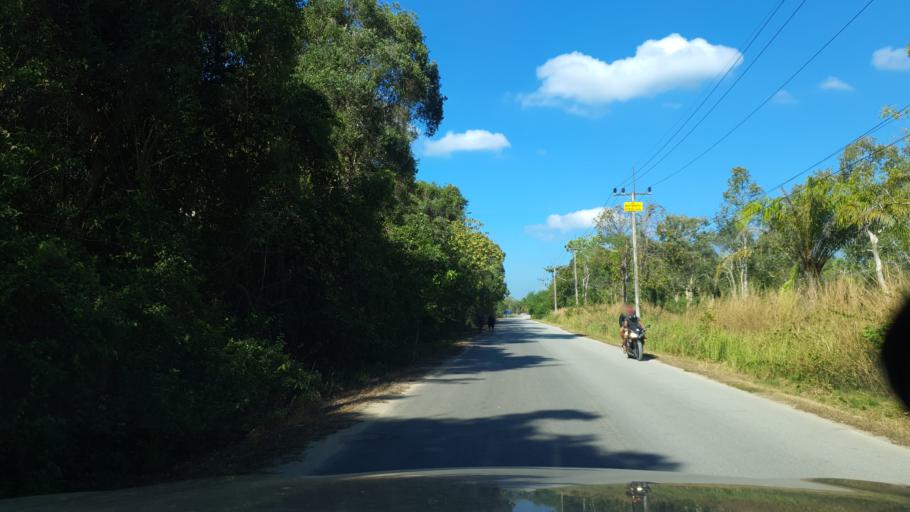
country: TH
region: Phangnga
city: Ban Ao Nang
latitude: 8.0493
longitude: 98.8037
